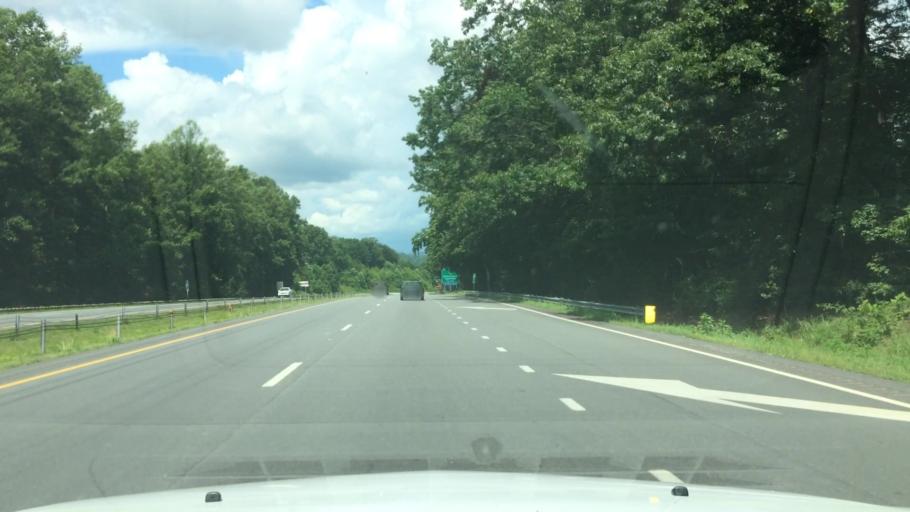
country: US
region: North Carolina
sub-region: Wilkes County
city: Wilkesboro
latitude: 36.1377
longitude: -81.1658
